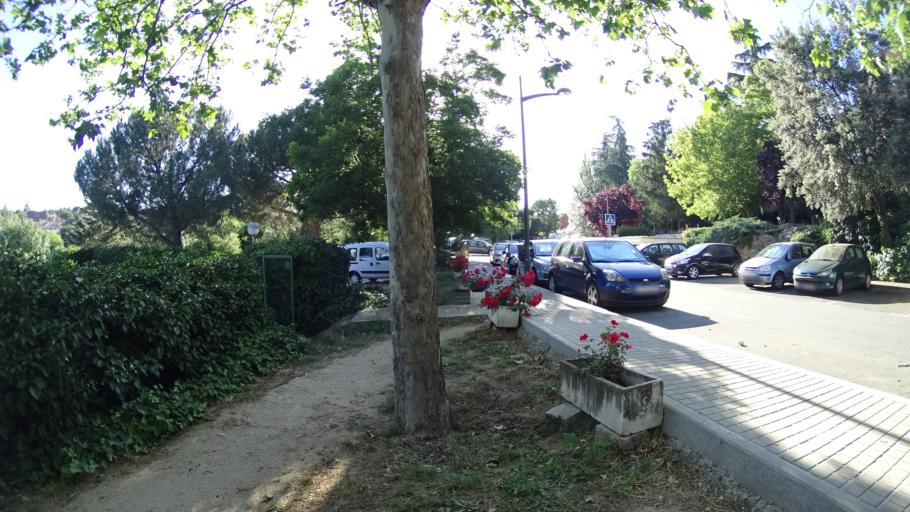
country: ES
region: Madrid
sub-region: Provincia de Madrid
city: Galapagar
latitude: 40.5982
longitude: -3.9798
